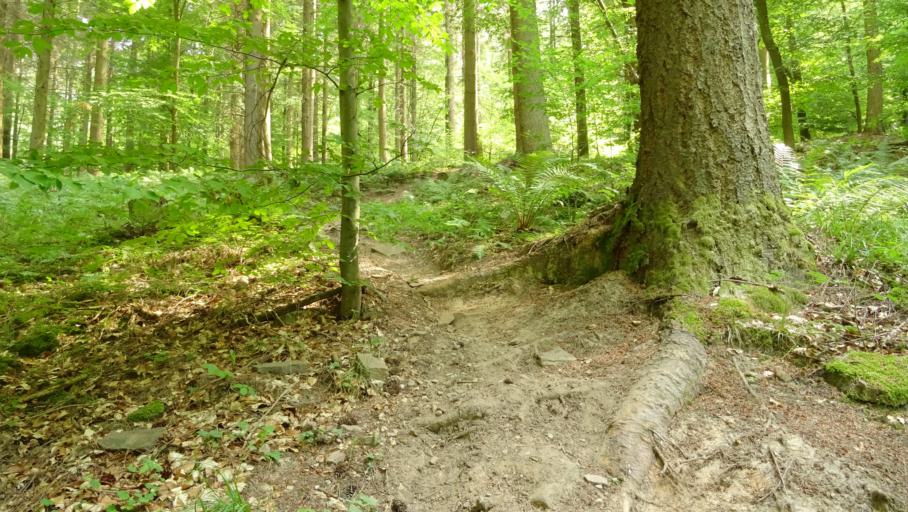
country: DE
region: Baden-Wuerttemberg
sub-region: Karlsruhe Region
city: Neckargerach
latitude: 49.4023
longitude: 9.0890
